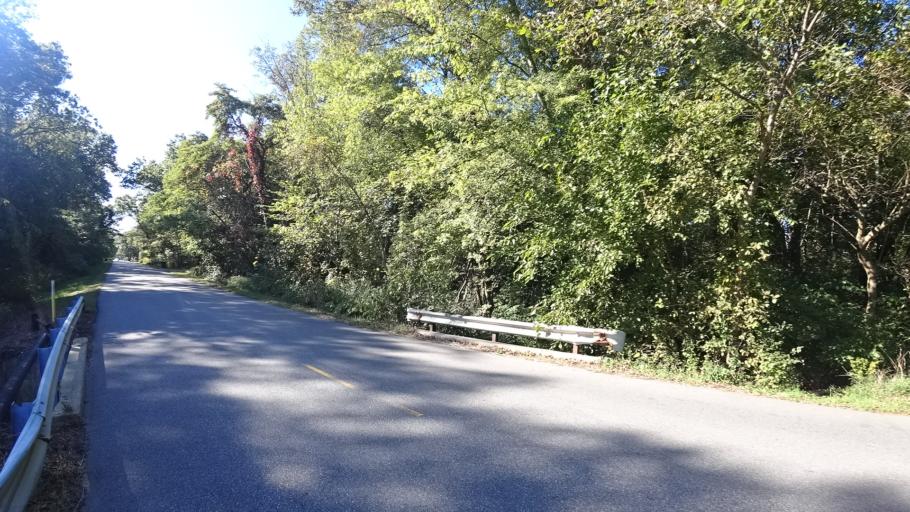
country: US
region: Indiana
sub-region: LaPorte County
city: Michigan City
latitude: 41.6942
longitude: -86.9324
